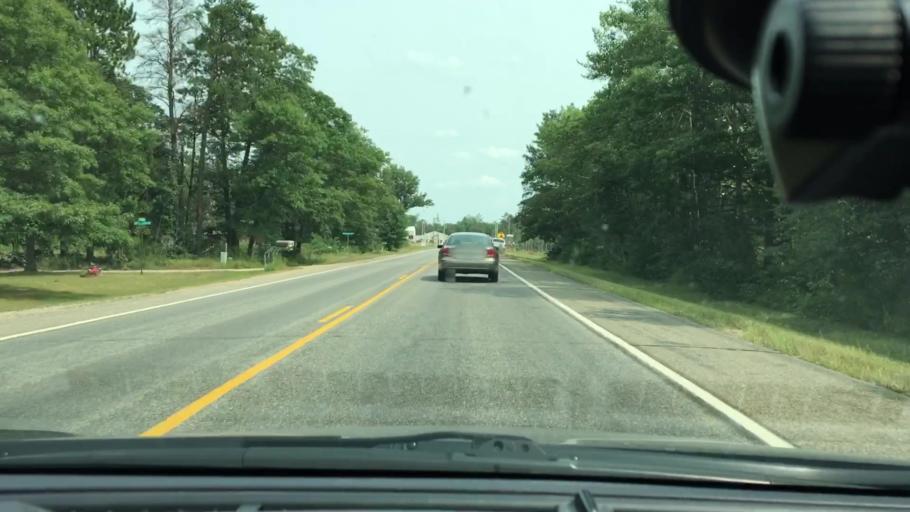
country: US
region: Minnesota
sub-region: Cass County
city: East Gull Lake
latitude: 46.4127
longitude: -94.2903
